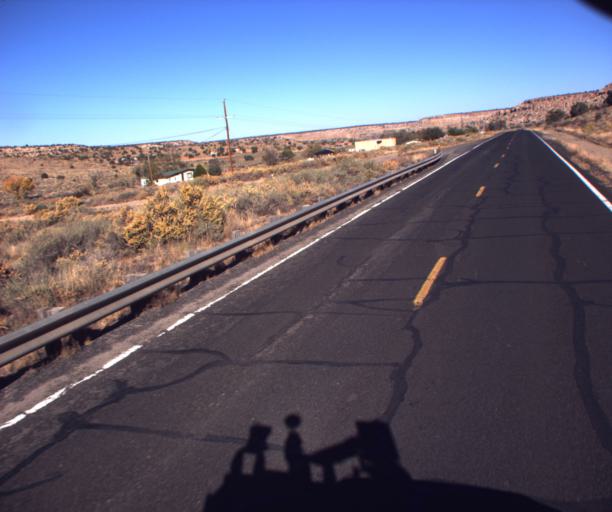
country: US
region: Arizona
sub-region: Navajo County
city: First Mesa
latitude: 35.8194
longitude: -110.2172
